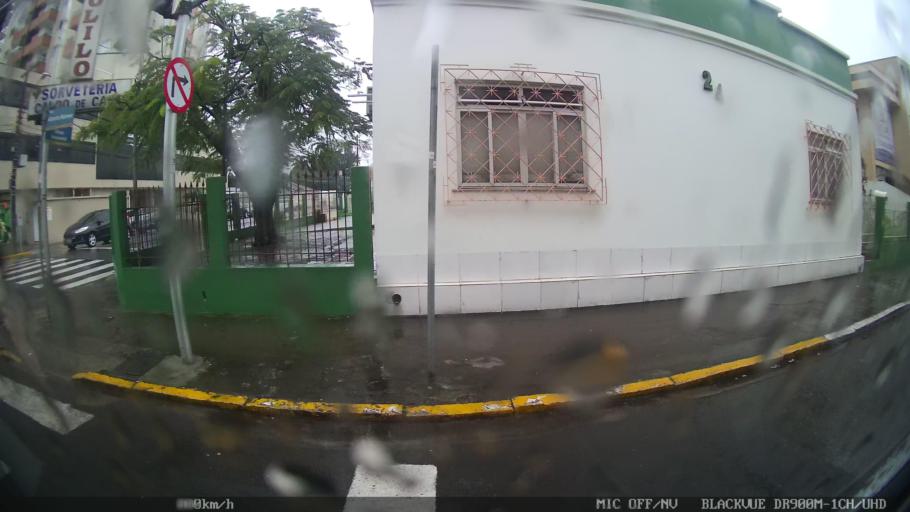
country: BR
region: Santa Catarina
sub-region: Itajai
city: Itajai
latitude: -26.9076
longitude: -48.6692
